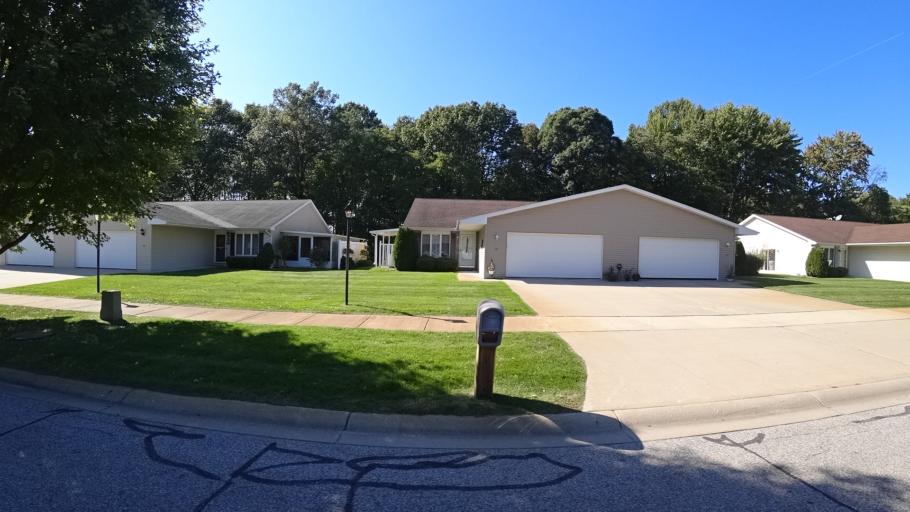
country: US
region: Indiana
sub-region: LaPorte County
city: Michigan City
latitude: 41.6863
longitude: -86.9079
